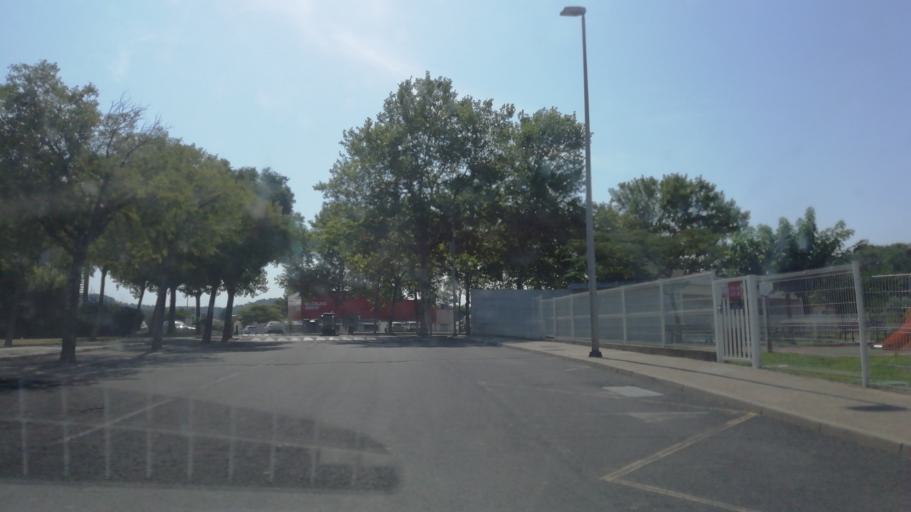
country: FR
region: Languedoc-Roussillon
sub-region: Departement de l'Herault
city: Saint-Mathieu-de-Treviers
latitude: 43.7665
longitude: 3.8619
